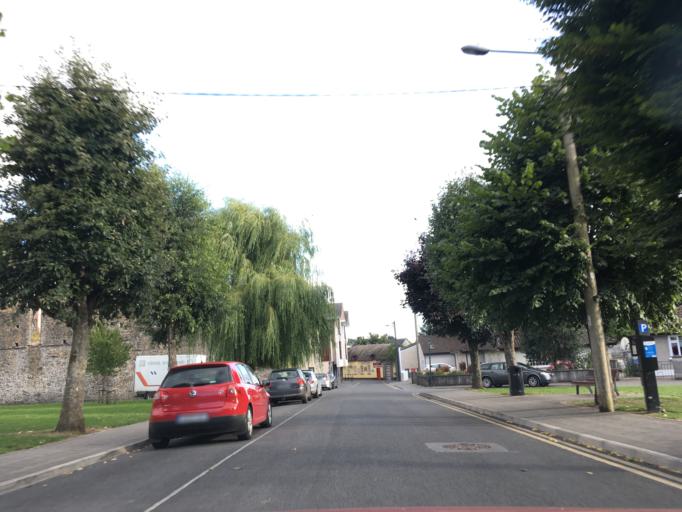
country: IE
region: Munster
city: Cashel
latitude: 52.5185
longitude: -7.8882
